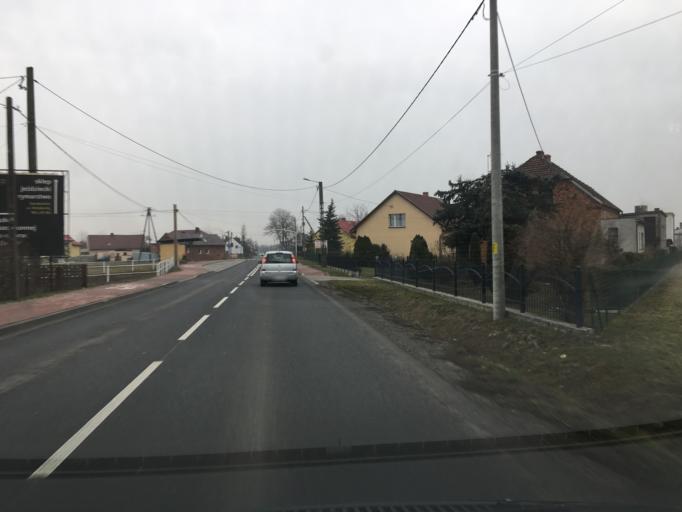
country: PL
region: Opole Voivodeship
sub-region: Powiat kedzierzynsko-kozielski
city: Kedzierzyn-Kozle
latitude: 50.3168
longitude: 18.2244
